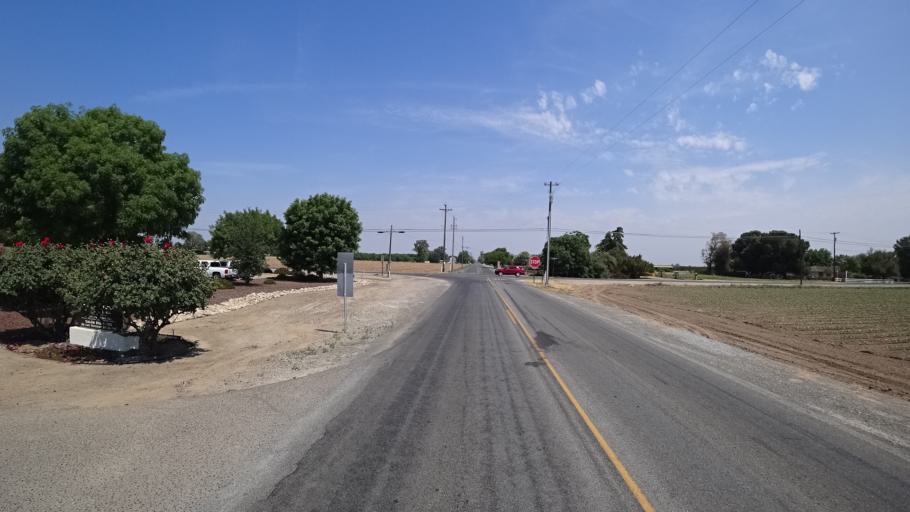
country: US
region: California
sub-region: Kings County
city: Lemoore
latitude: 36.3130
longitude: -119.7628
